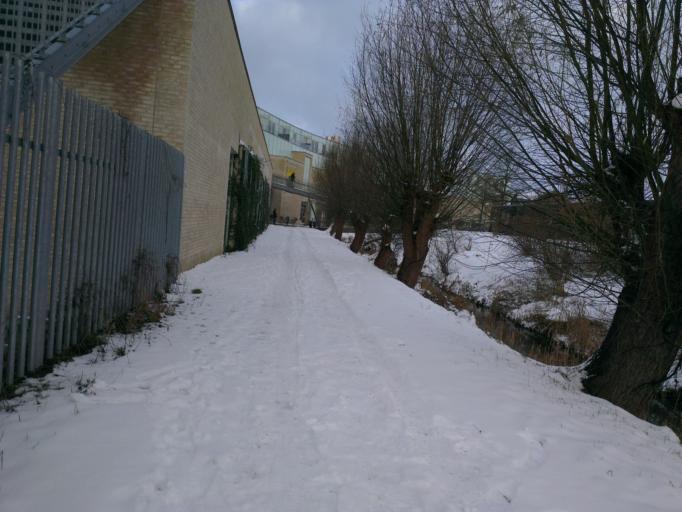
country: DK
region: Capital Region
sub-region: Frederikssund Kommune
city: Frederikssund
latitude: 55.8353
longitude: 12.0652
